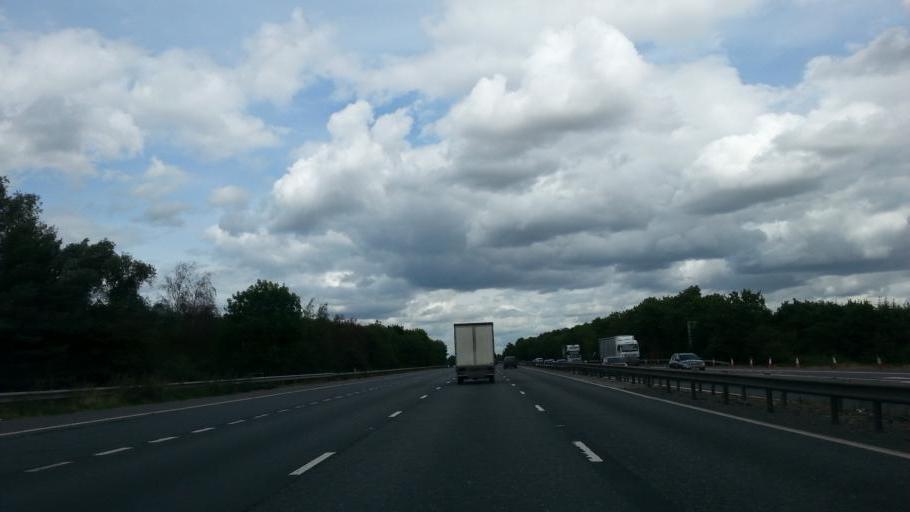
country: GB
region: England
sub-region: Essex
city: Harlow
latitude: 51.7468
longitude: 0.1401
